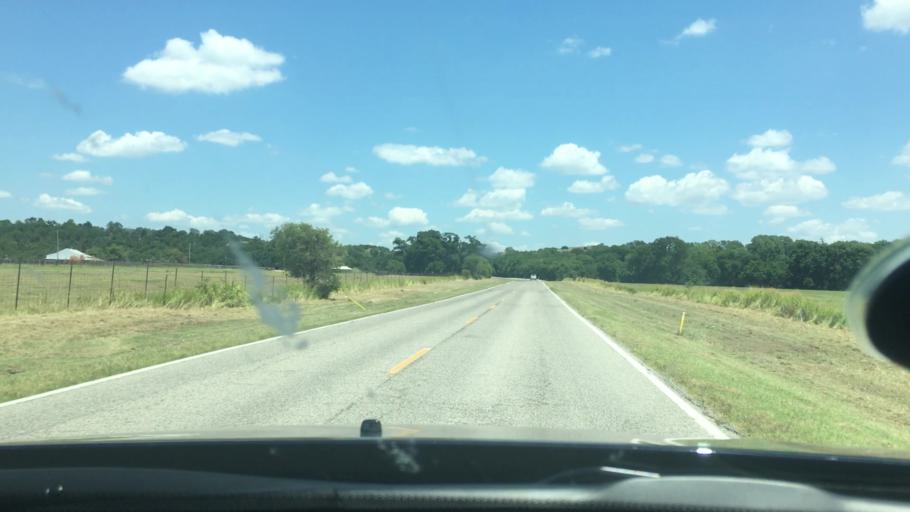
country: US
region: Oklahoma
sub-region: Carter County
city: Dickson
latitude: 34.3025
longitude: -96.9645
